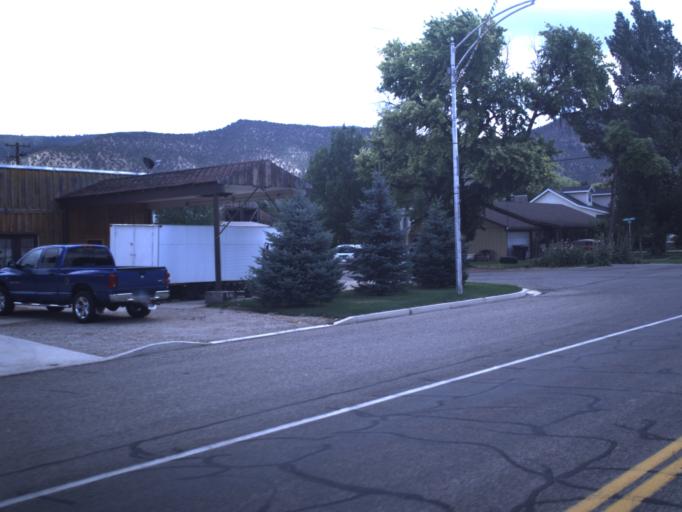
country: US
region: Utah
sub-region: Iron County
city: Parowan
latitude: 37.8864
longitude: -112.7751
